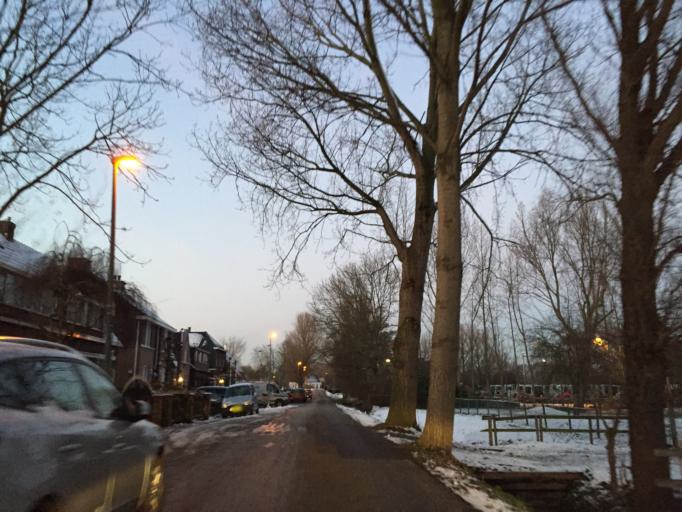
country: NL
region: South Holland
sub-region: Gemeente Schiedam
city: Schiedam
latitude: 51.9449
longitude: 4.3878
